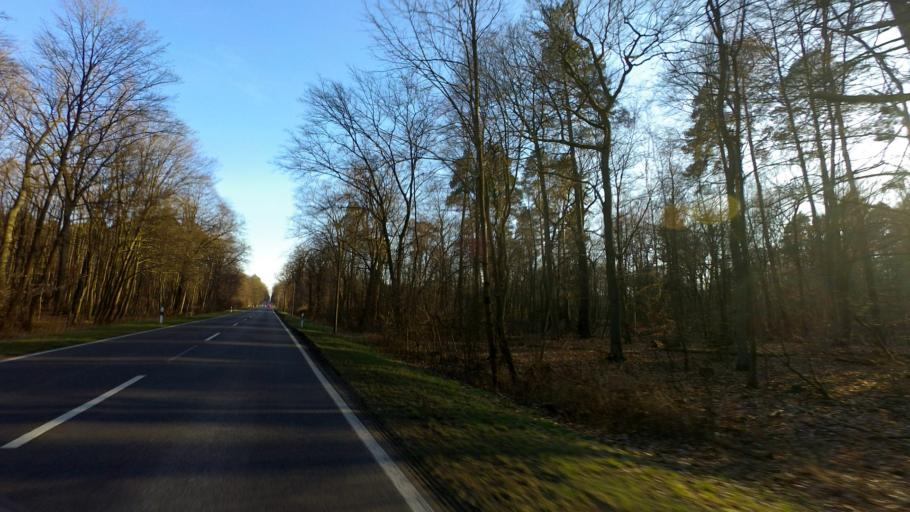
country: DE
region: Brandenburg
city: Eberswalde
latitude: 52.8176
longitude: 13.8325
